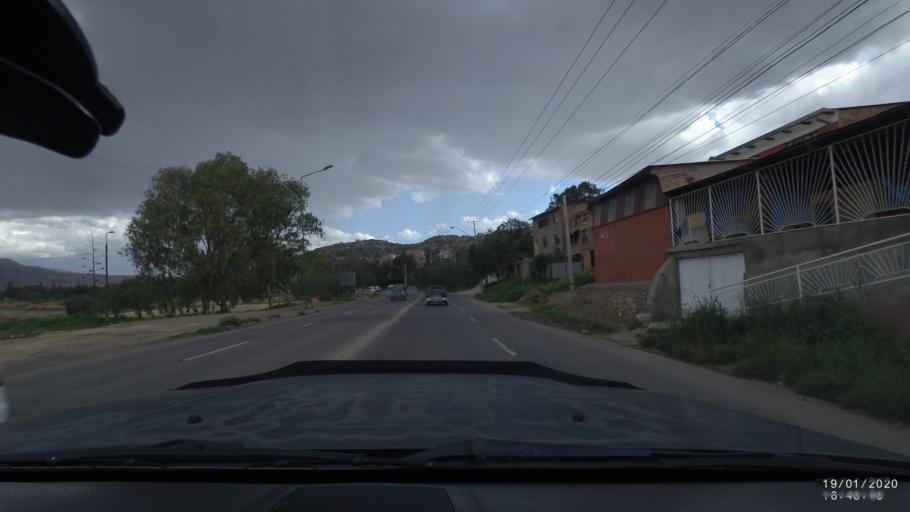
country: BO
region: Cochabamba
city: Cochabamba
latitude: -17.4130
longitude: -66.1425
